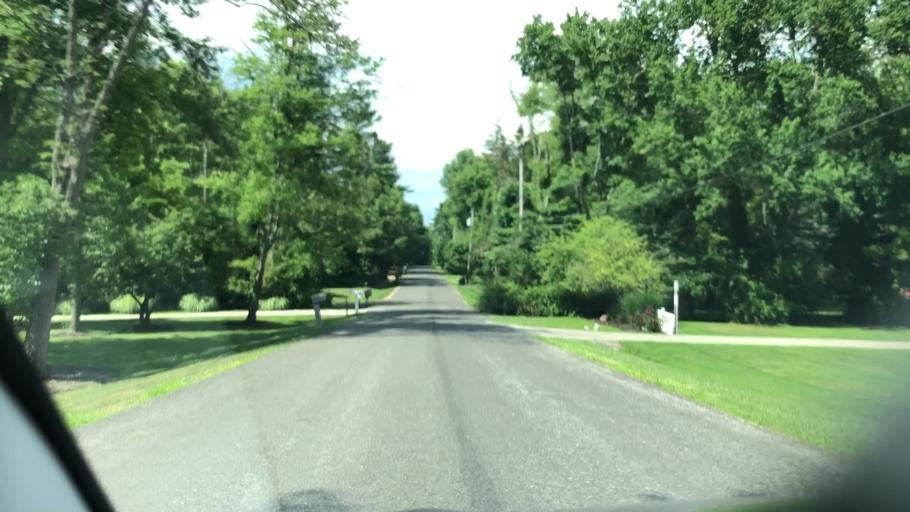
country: US
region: Ohio
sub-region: Summit County
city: Montrose-Ghent
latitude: 41.1531
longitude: -81.6504
